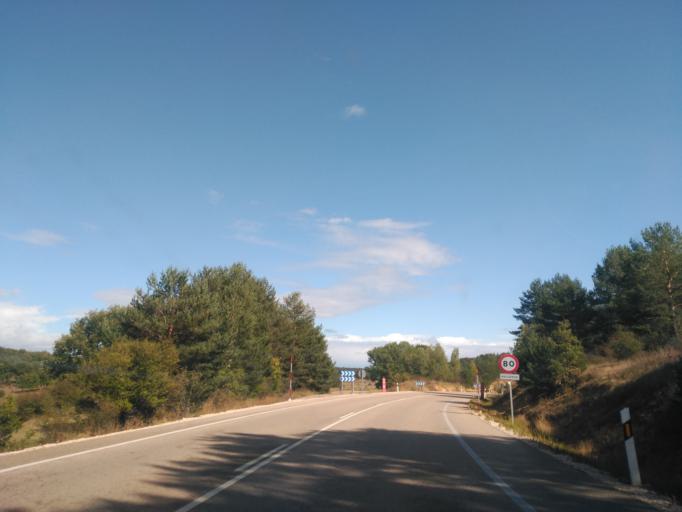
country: ES
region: Castille and Leon
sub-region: Provincia de Burgos
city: Rabanera del Pinar
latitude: 41.8855
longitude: -3.2326
